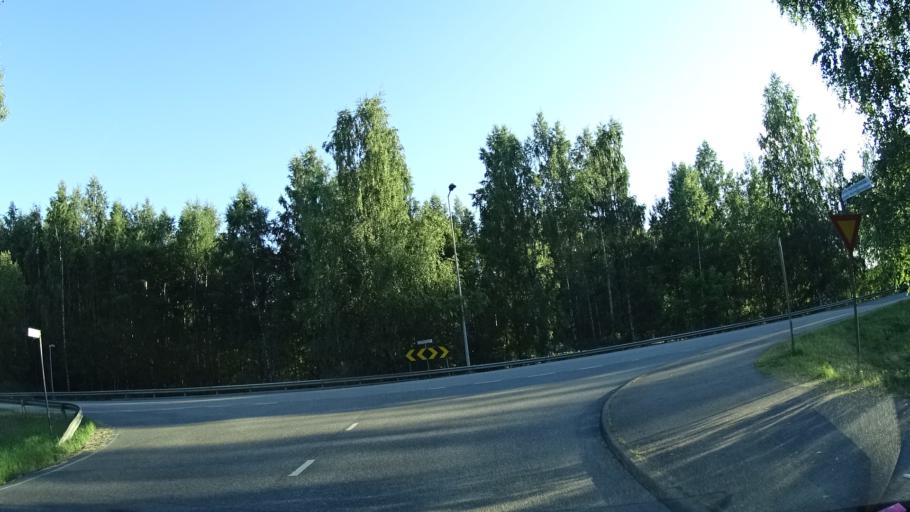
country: FI
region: Uusimaa
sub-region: Helsinki
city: Teekkarikylae
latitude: 60.2739
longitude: 24.8743
